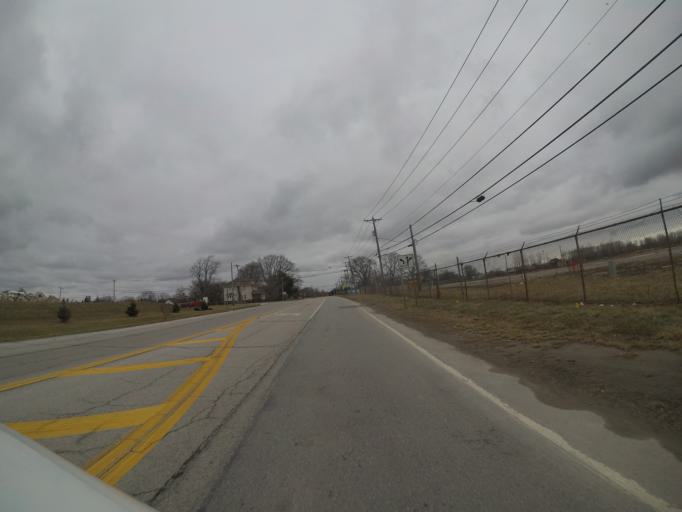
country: US
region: Ohio
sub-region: Wood County
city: Walbridge
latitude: 41.6151
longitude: -83.5125
